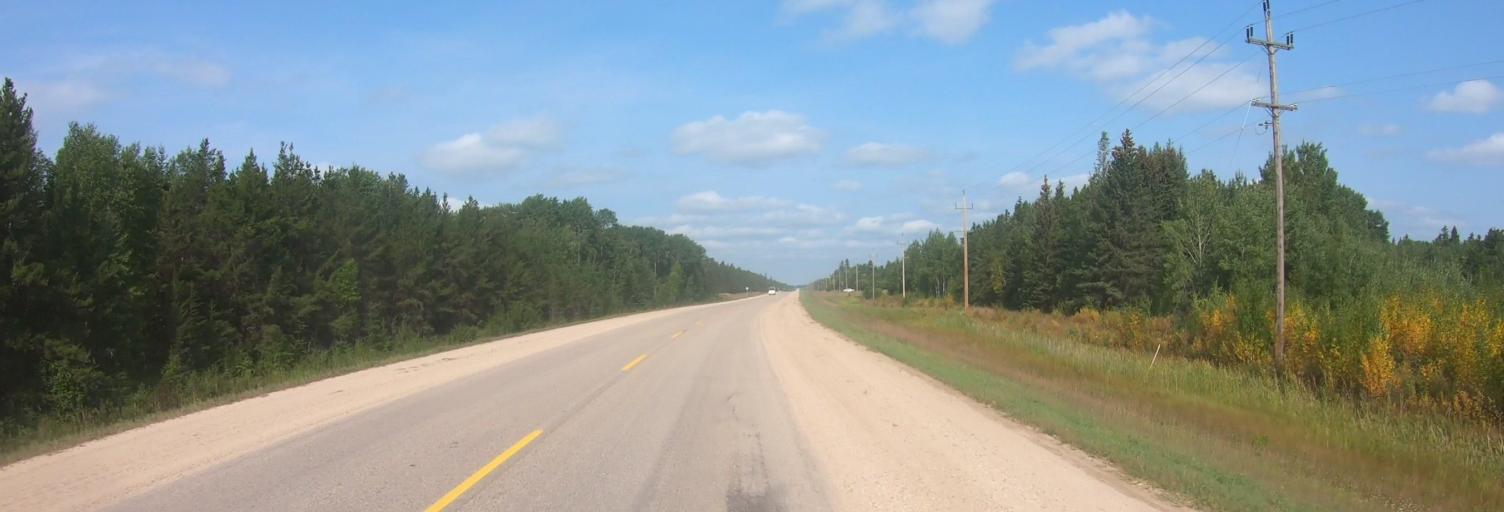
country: CA
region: Manitoba
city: La Broquerie
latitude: 49.1872
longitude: -96.2502
